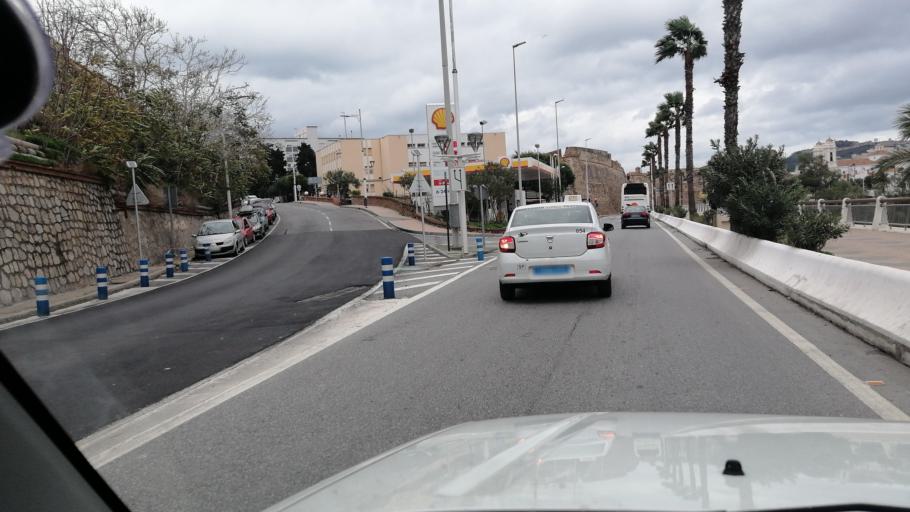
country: ES
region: Ceuta
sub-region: Ceuta
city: Ceuta
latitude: 35.8865
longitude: -5.3213
